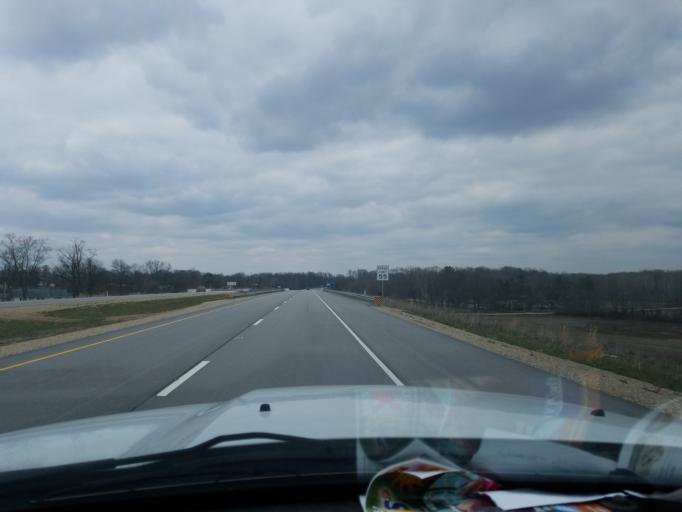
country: US
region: Indiana
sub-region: Vigo County
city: Terre Haute
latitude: 39.4036
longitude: -87.3674
